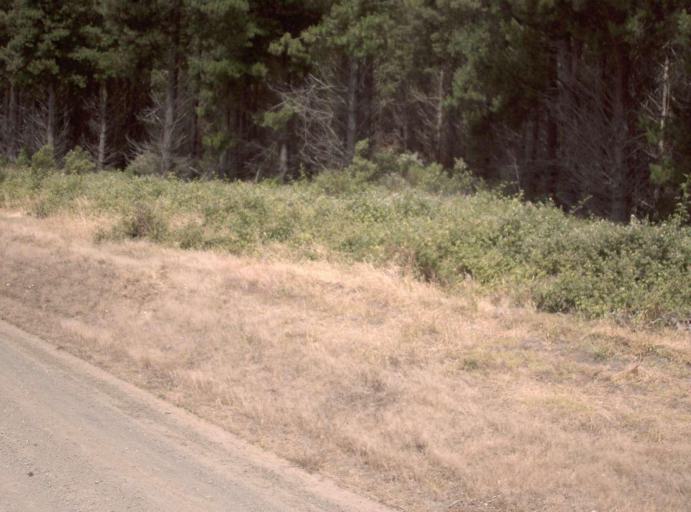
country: AU
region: Victoria
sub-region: Latrobe
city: Traralgon
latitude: -38.3992
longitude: 146.6523
